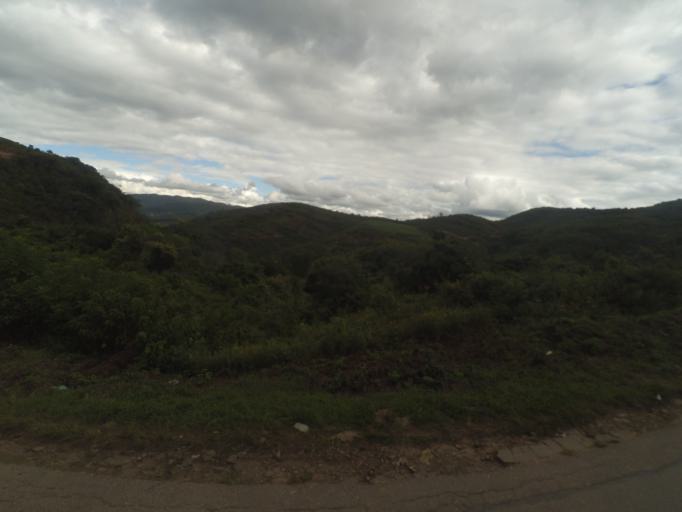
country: BO
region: Santa Cruz
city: Samaipata
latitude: -18.1746
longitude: -63.8530
